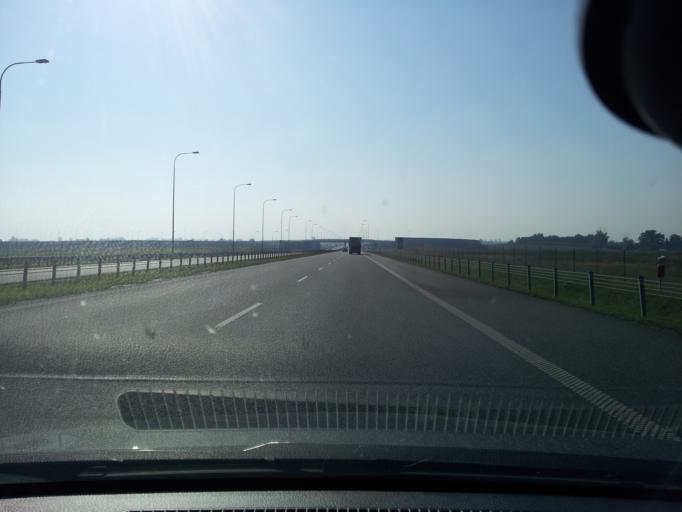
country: PL
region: Kujawsko-Pomorskie
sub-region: Powiat torunski
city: Lubicz Dolny
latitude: 53.0953
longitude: 18.7495
